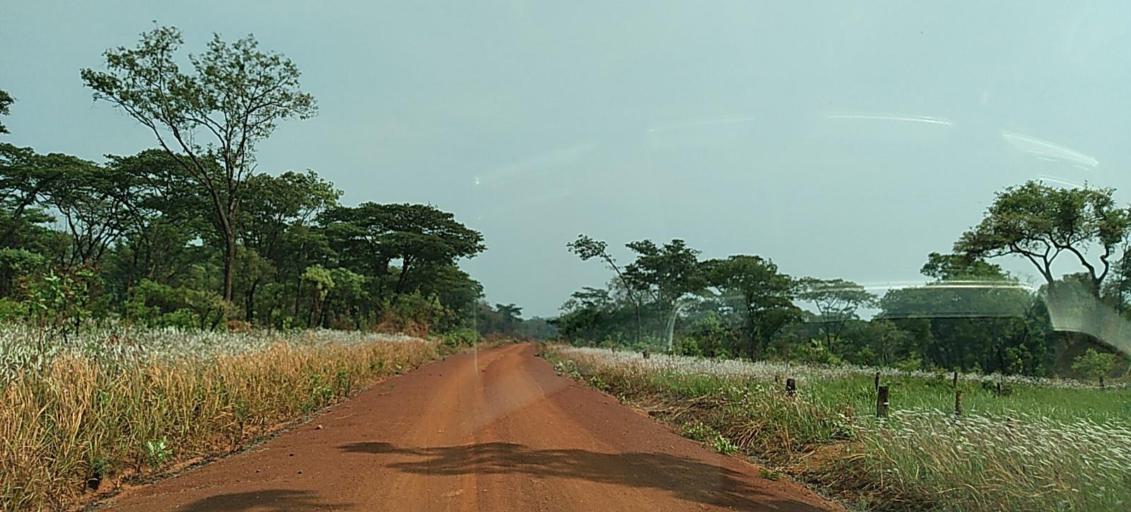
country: ZM
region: North-Western
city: Kansanshi
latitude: -12.0225
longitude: 26.8505
